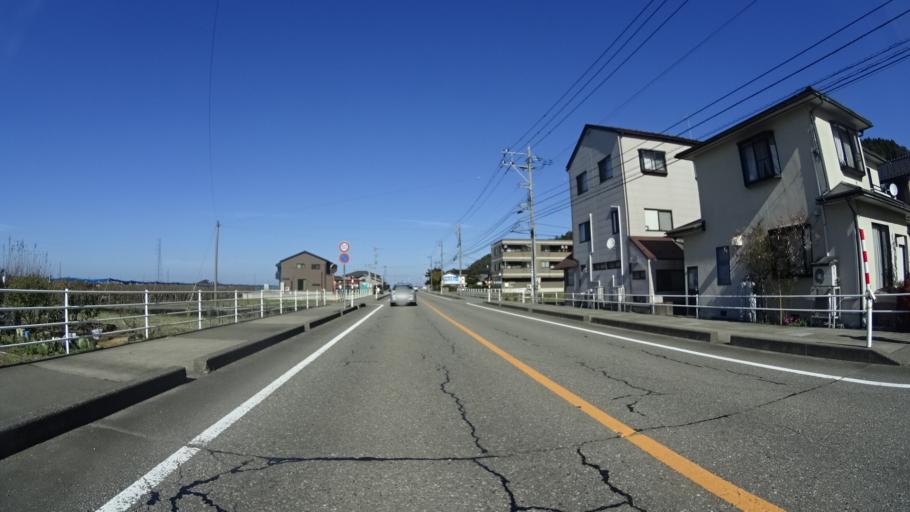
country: JP
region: Ishikawa
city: Tsurugi-asahimachi
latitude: 36.4589
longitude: 136.6219
